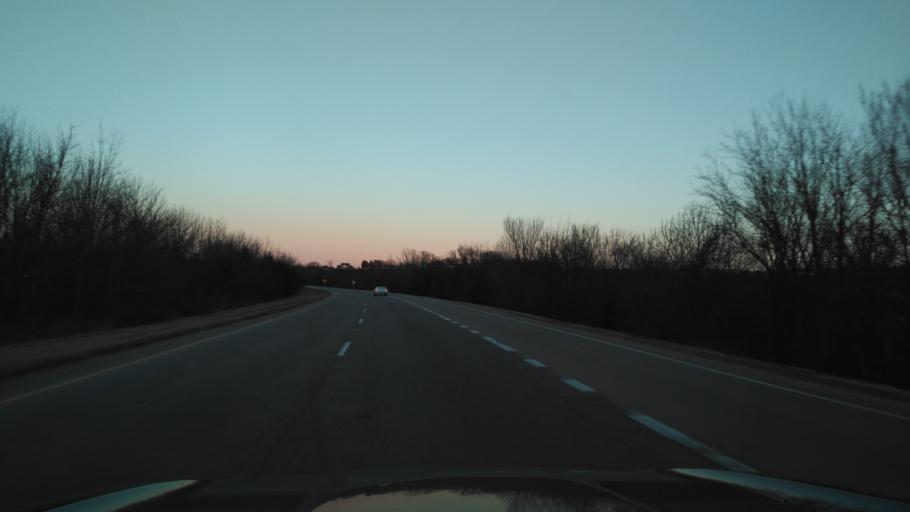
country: US
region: Arkansas
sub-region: Crawford County
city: Van Buren
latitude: 35.4601
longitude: -94.3898
